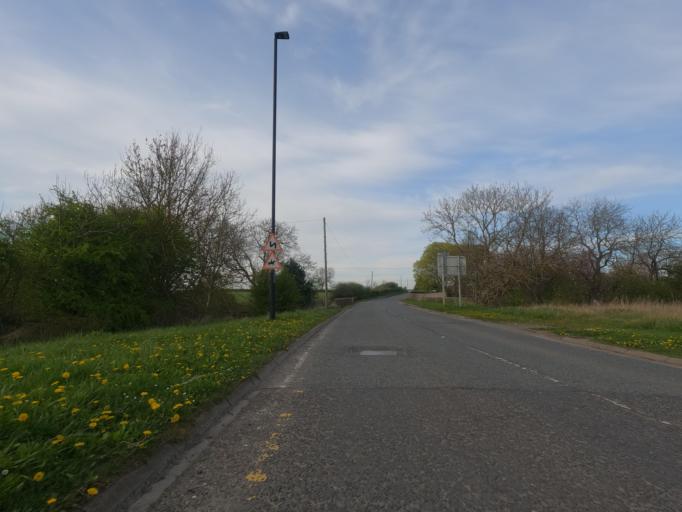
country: GB
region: England
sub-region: Newcastle upon Tyne
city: Dinnington
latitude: 55.0228
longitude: -1.6664
